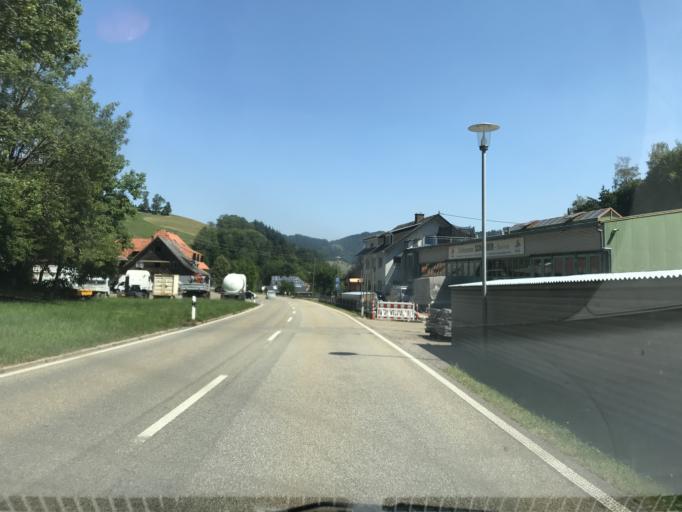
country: DE
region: Baden-Wuerttemberg
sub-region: Freiburg Region
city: Oberried
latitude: 47.9303
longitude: 7.9424
